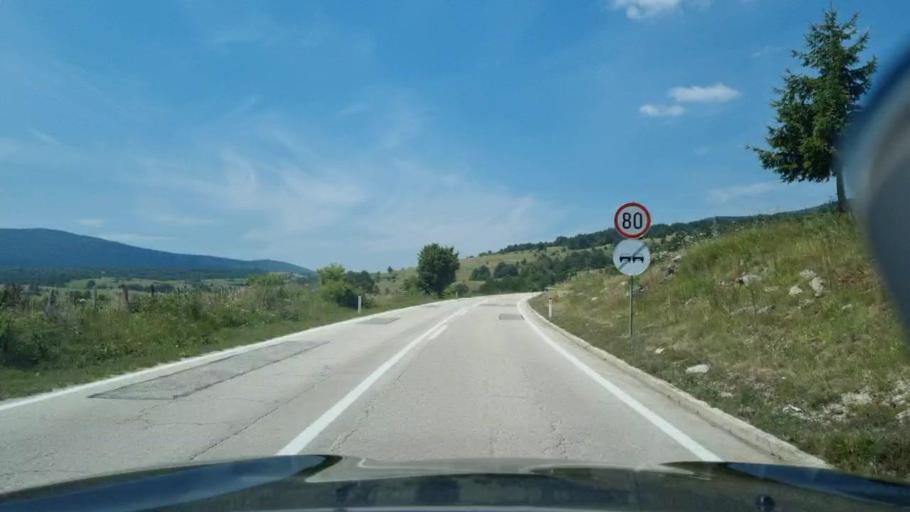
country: BA
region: Federation of Bosnia and Herzegovina
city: Sanica
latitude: 44.5471
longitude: 16.6042
